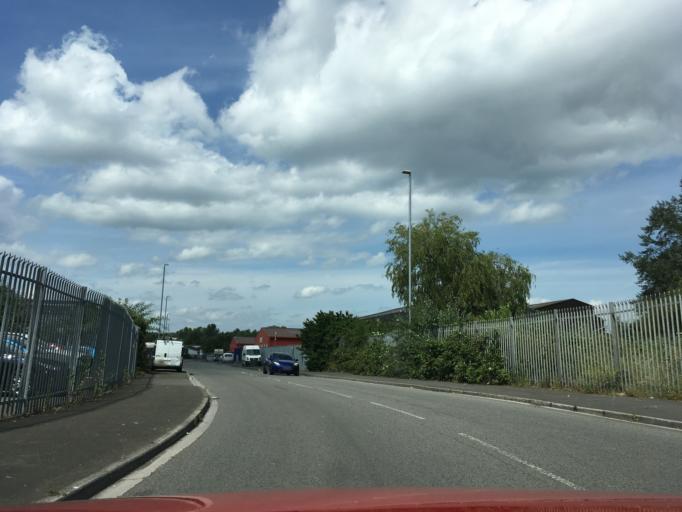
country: GB
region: Wales
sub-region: Newport
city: Nash
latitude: 51.5710
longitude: -2.9477
